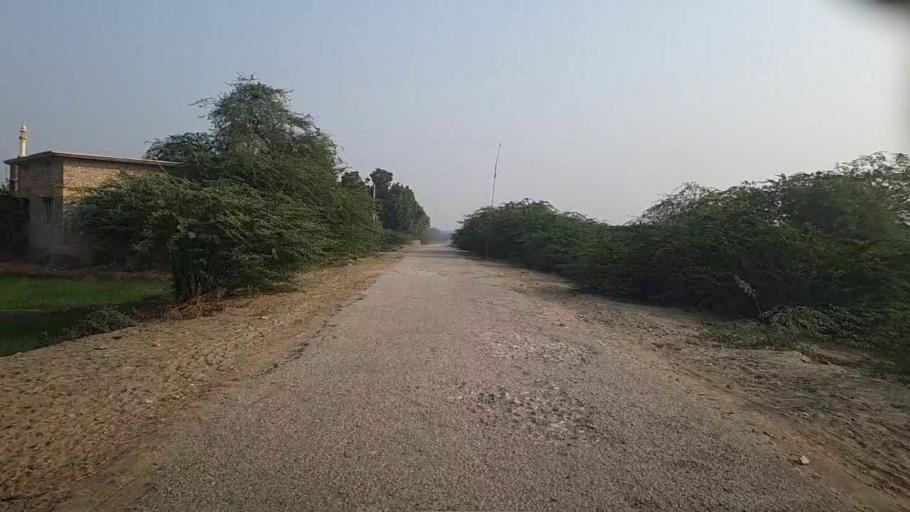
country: PK
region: Sindh
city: Kandiari
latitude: 27.0426
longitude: 68.4760
